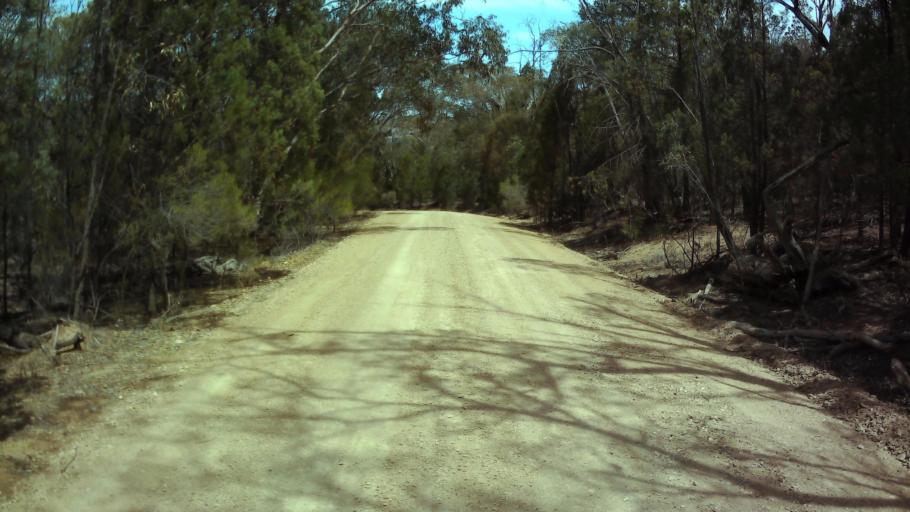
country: AU
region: New South Wales
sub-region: Weddin
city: Grenfell
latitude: -33.8129
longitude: 148.1621
